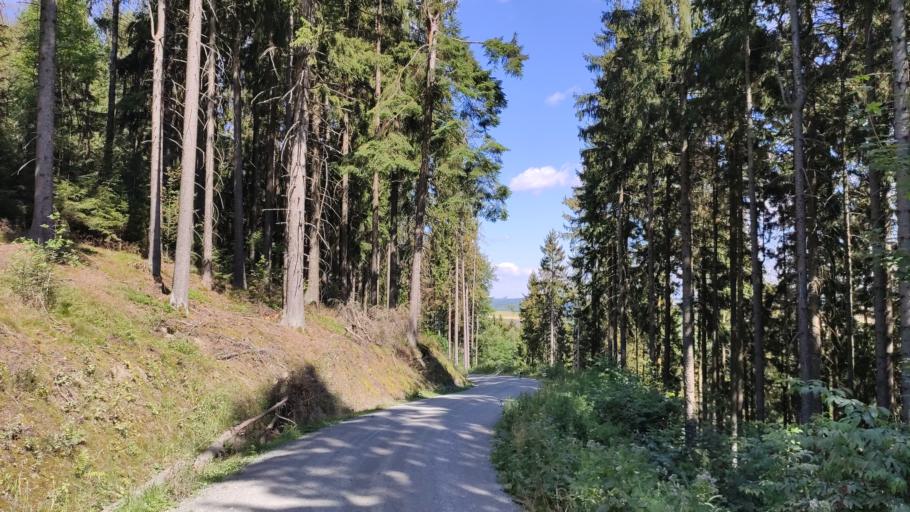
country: DE
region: Bavaria
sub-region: Upper Franconia
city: Ludwigsstadt
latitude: 50.4960
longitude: 11.4208
